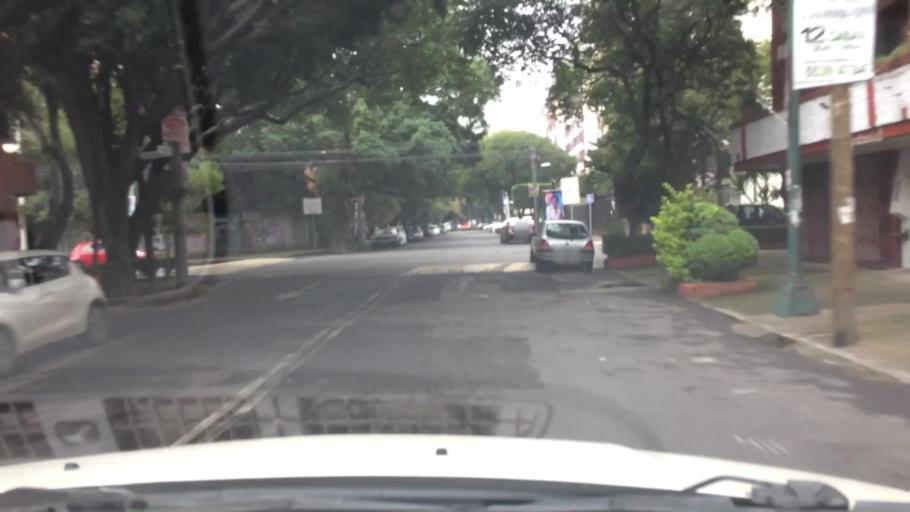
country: MX
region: Mexico City
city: Benito Juarez
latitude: 19.4000
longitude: -99.1655
